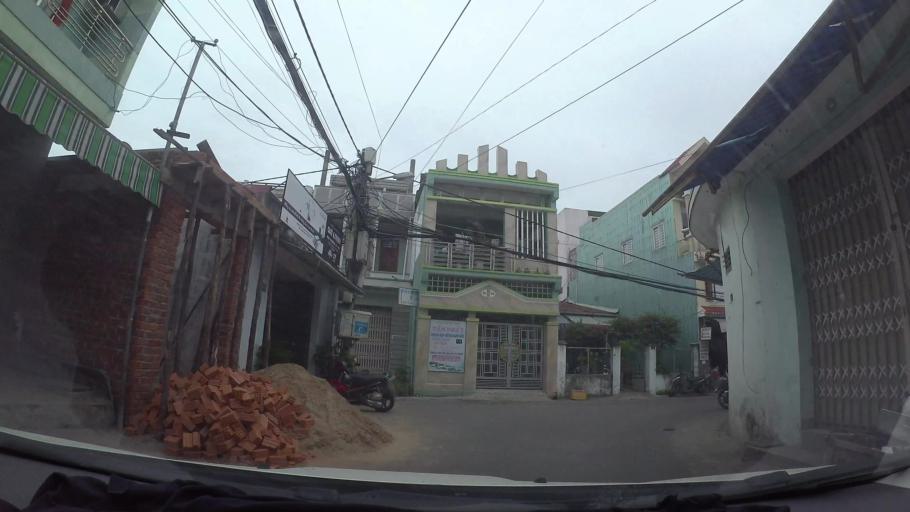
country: VN
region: Da Nang
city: Lien Chieu
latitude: 16.0730
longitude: 108.1459
